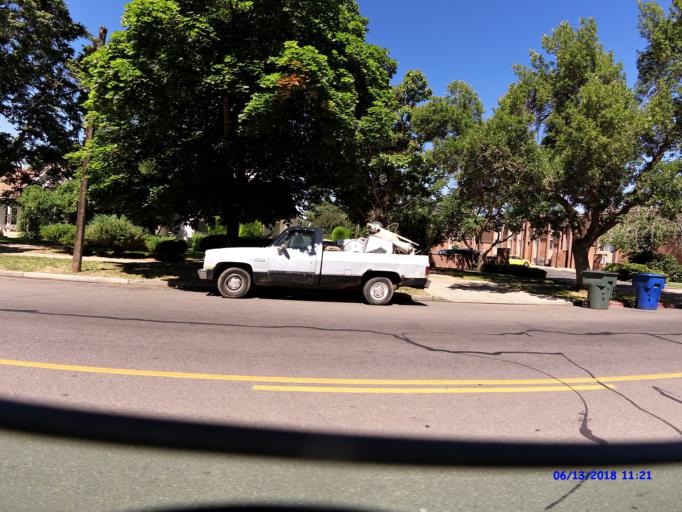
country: US
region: Utah
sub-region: Weber County
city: Ogden
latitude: 41.2254
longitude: -111.9592
